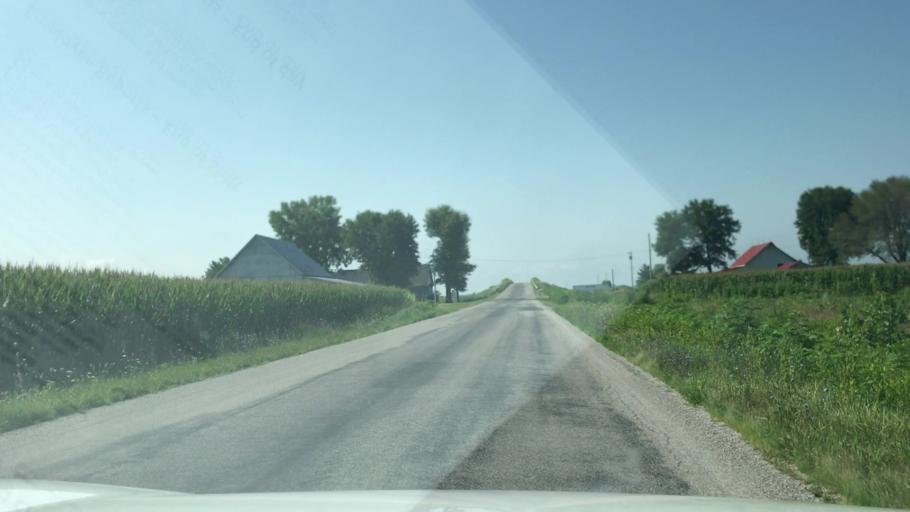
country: US
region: Illinois
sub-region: Washington County
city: Okawville
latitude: 38.4315
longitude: -89.4778
